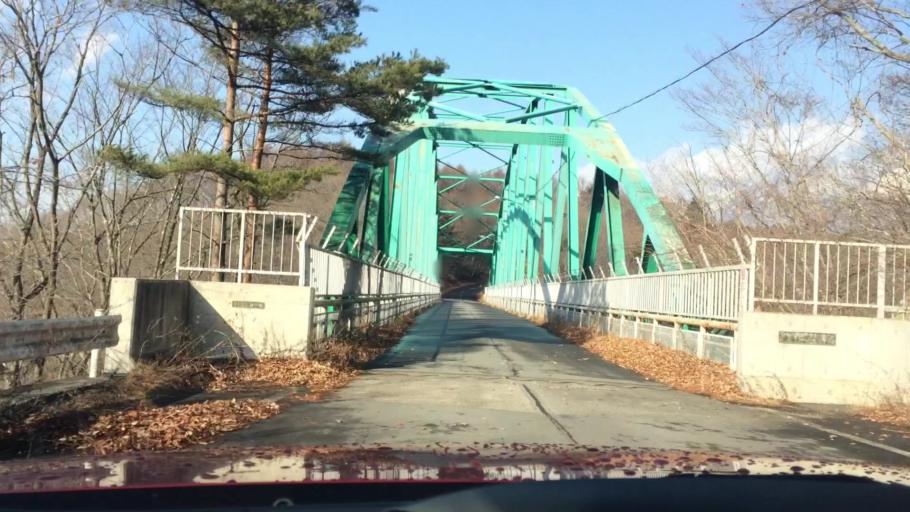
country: JP
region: Nagano
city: Komoro
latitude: 36.3141
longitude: 138.5517
